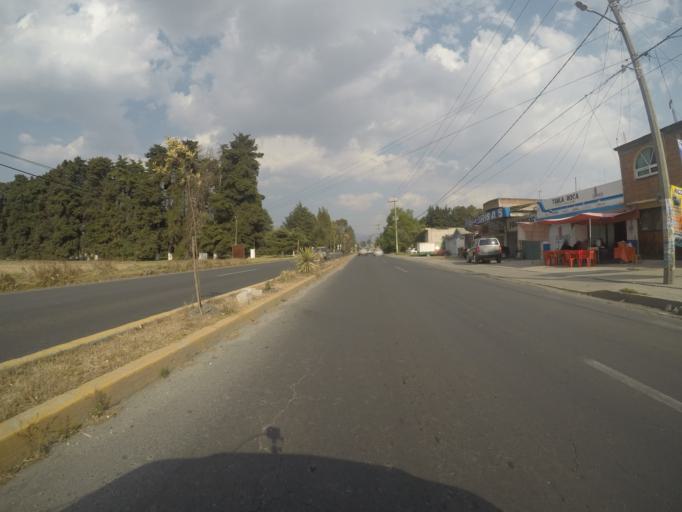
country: MX
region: Mexico
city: Santa Cruz Atizapan
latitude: 19.1836
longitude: -99.4910
